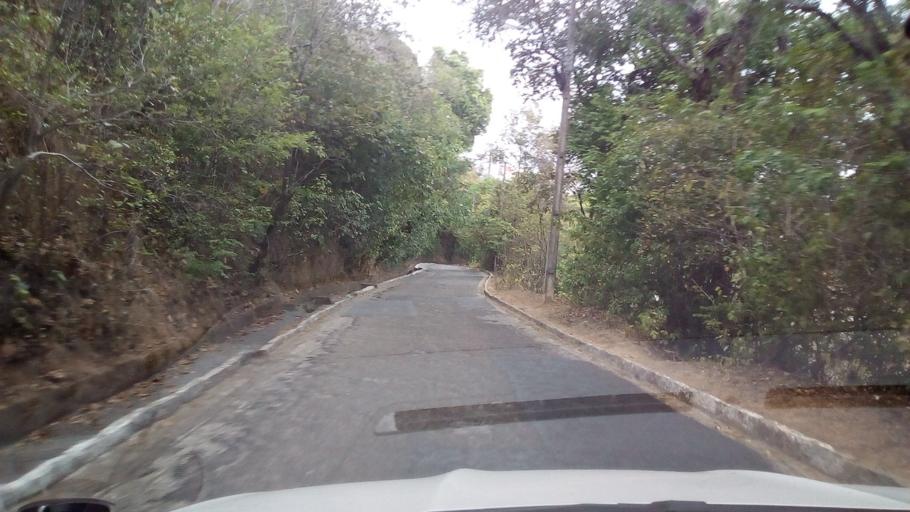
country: BR
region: Paraiba
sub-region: Joao Pessoa
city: Joao Pessoa
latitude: -7.1333
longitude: -34.8232
